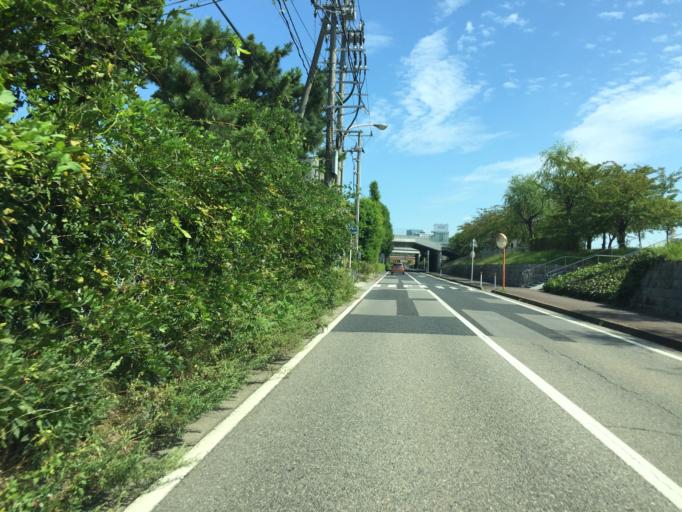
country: JP
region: Niigata
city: Niigata-shi
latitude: 37.9118
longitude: 139.0391
